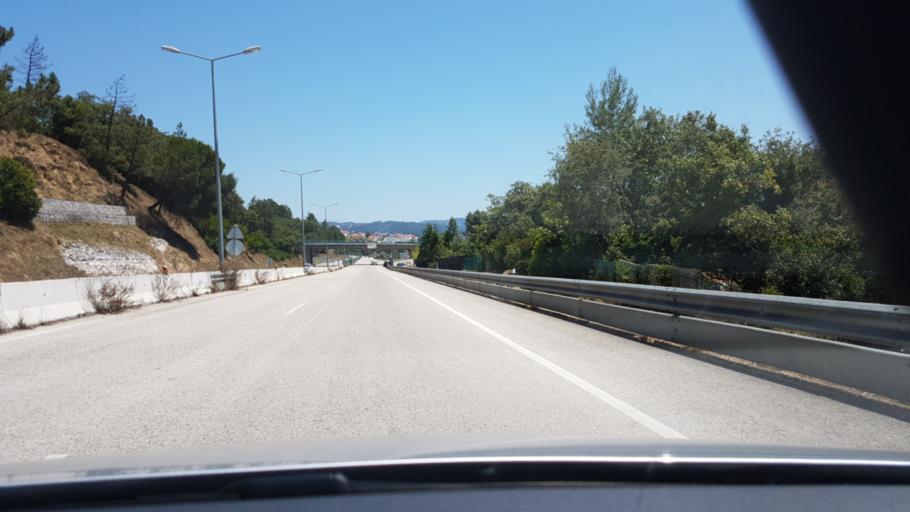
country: PT
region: Coimbra
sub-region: Coimbra
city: Coimbra
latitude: 40.1801
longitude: -8.4460
